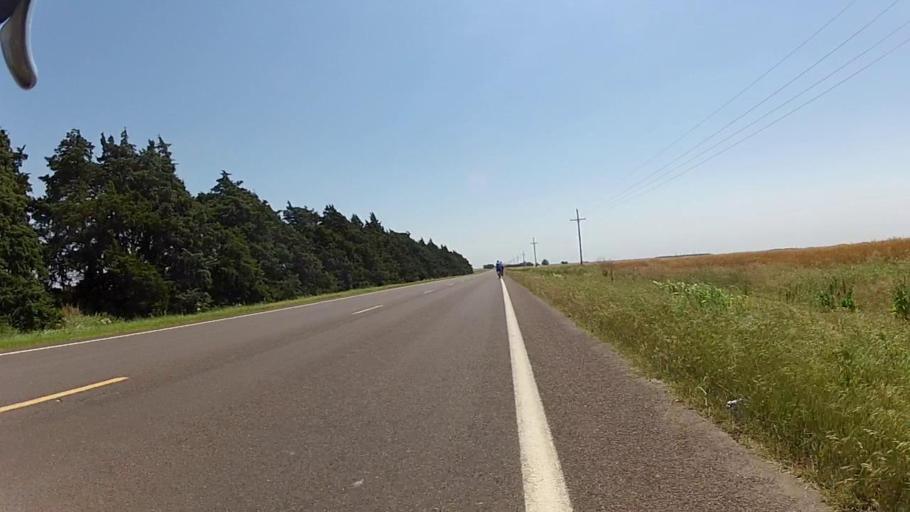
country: US
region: Kansas
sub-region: Sumner County
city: Caldwell
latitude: 37.0330
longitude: -97.5580
